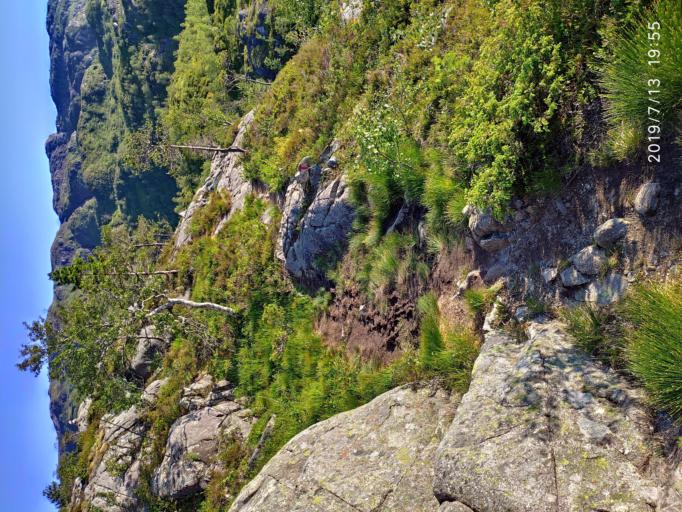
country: NO
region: Rogaland
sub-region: Sauda
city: Sauda
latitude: 59.8409
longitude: 6.3480
